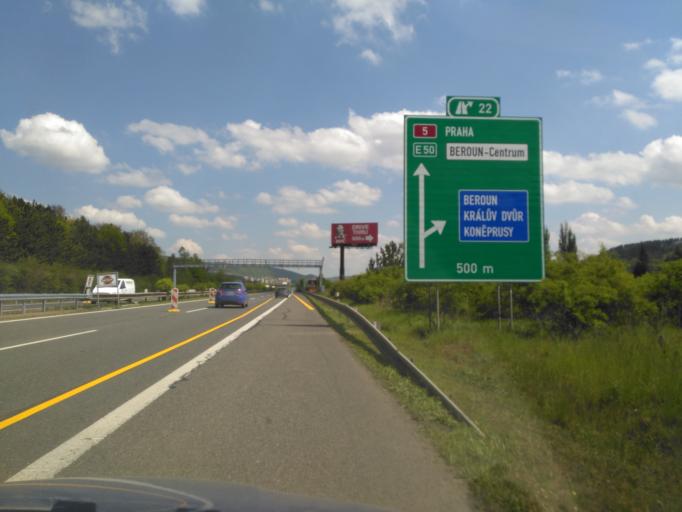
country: CZ
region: Central Bohemia
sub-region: Okres Beroun
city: Kraluv Dvur
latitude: 49.9277
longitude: 14.0133
